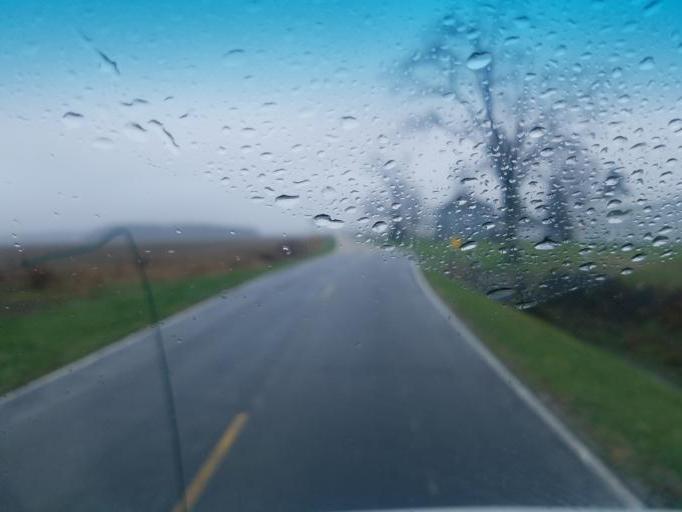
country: US
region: Ohio
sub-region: Wood County
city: North Baltimore
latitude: 41.1679
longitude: -83.6312
